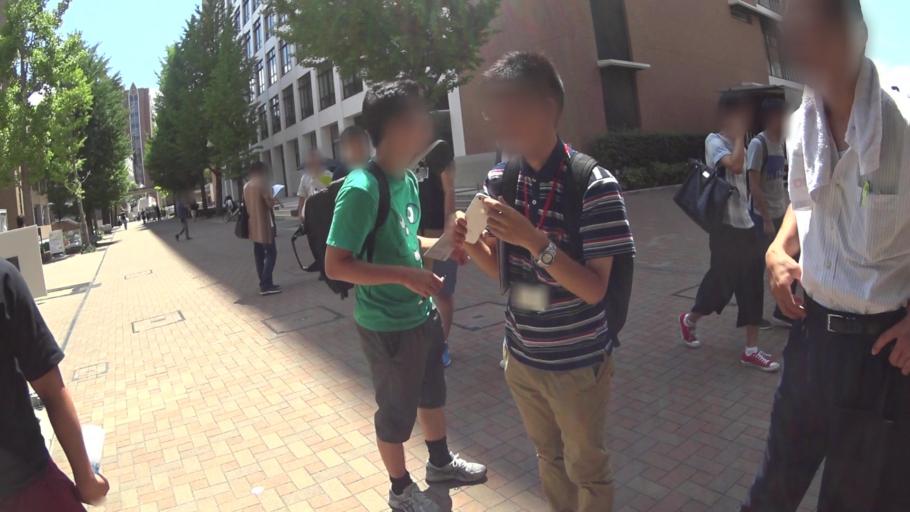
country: JP
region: Osaka
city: Yao
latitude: 34.6521
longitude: 135.5896
